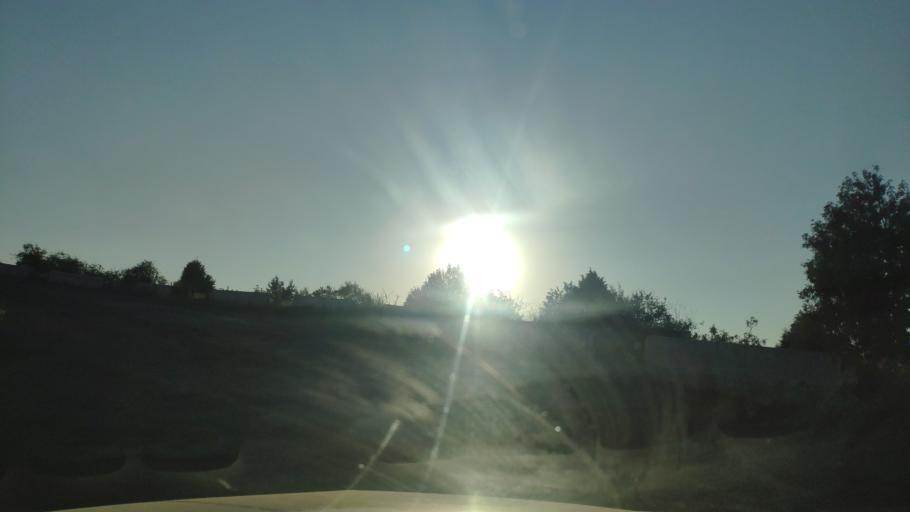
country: TJ
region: Viloyati Sughd
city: Ayni
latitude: 39.6419
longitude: 68.4699
